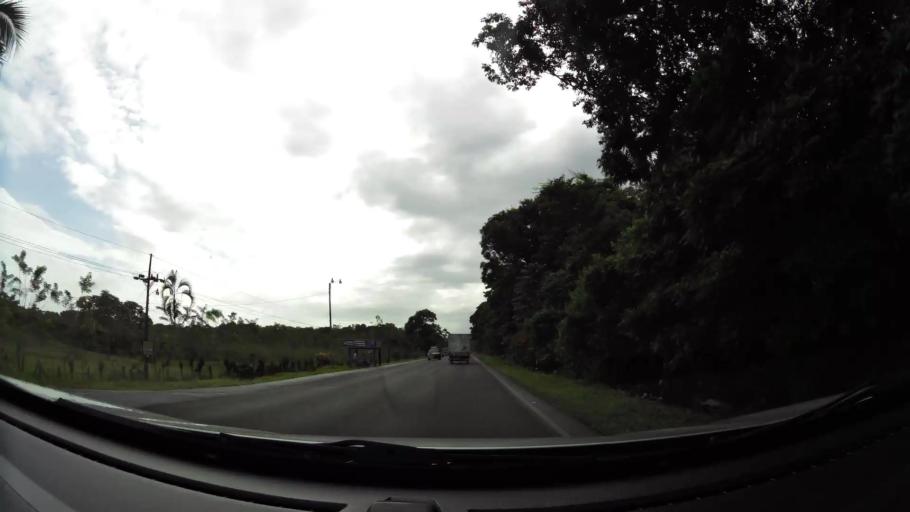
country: CR
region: Limon
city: Pocora
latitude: 10.1790
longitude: -83.6208
